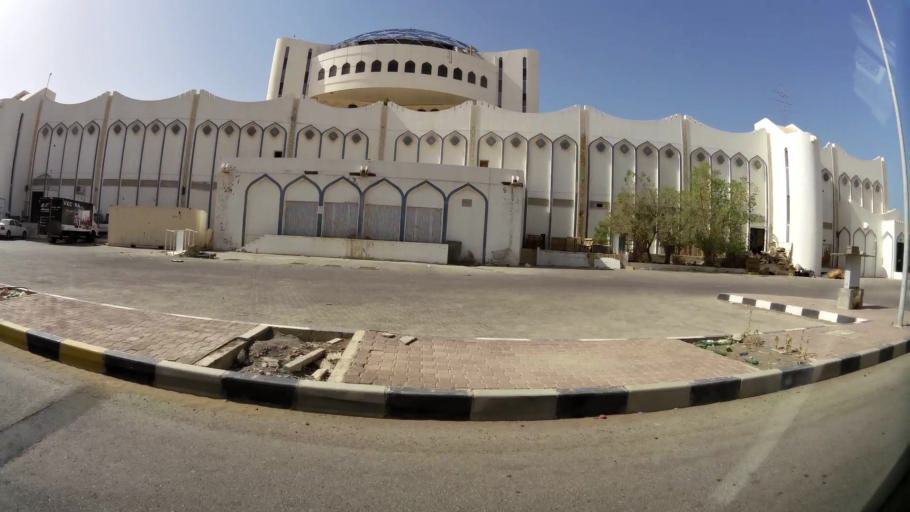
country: OM
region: Muhafazat Masqat
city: Muscat
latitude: 23.6064
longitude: 58.5003
